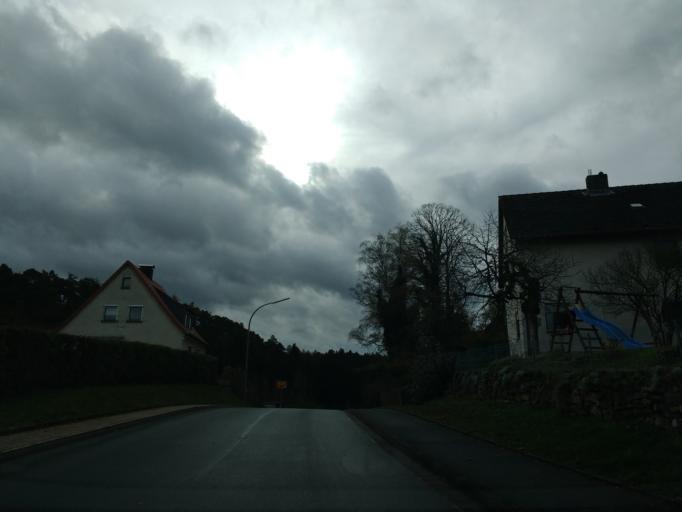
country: DE
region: Hesse
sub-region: Regierungsbezirk Kassel
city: Vohl
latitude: 51.2015
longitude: 8.9412
